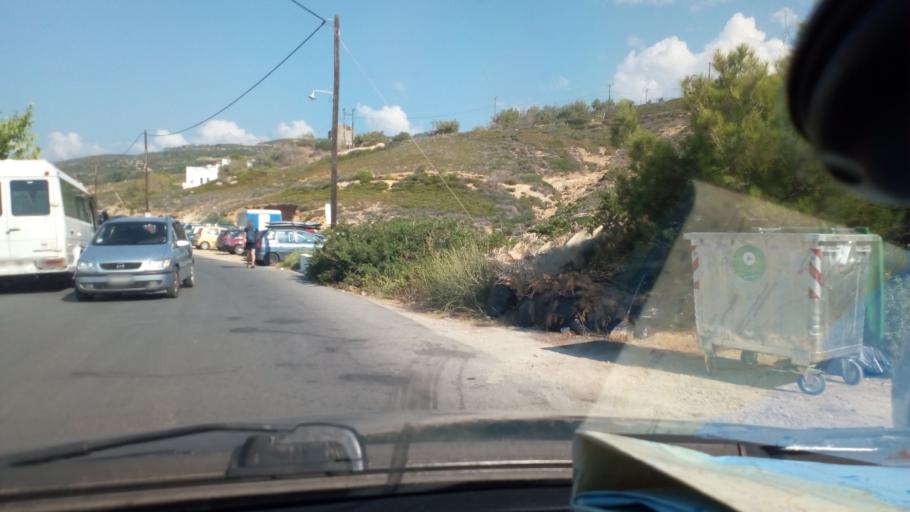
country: GR
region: North Aegean
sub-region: Nomos Samou
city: Agios Kirykos
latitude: 37.6300
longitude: 26.0946
